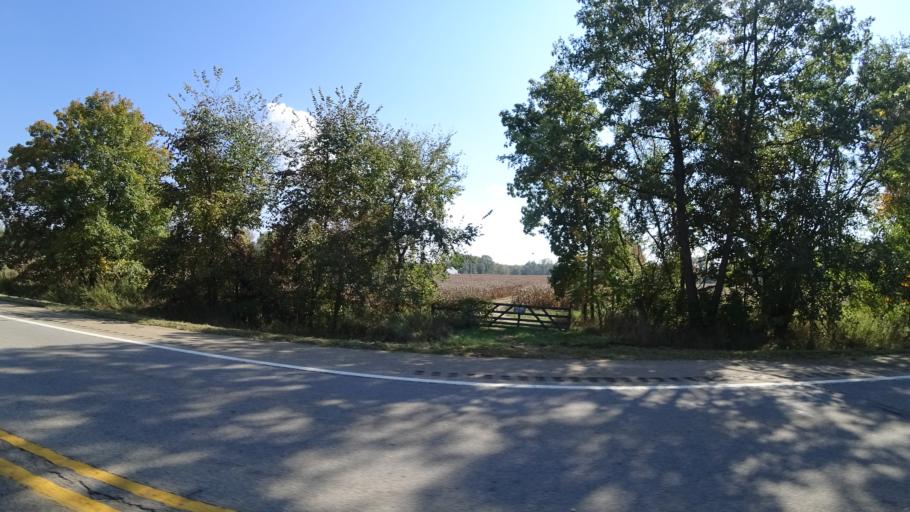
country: US
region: Michigan
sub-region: Calhoun County
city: Homer
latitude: 42.1582
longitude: -84.7731
